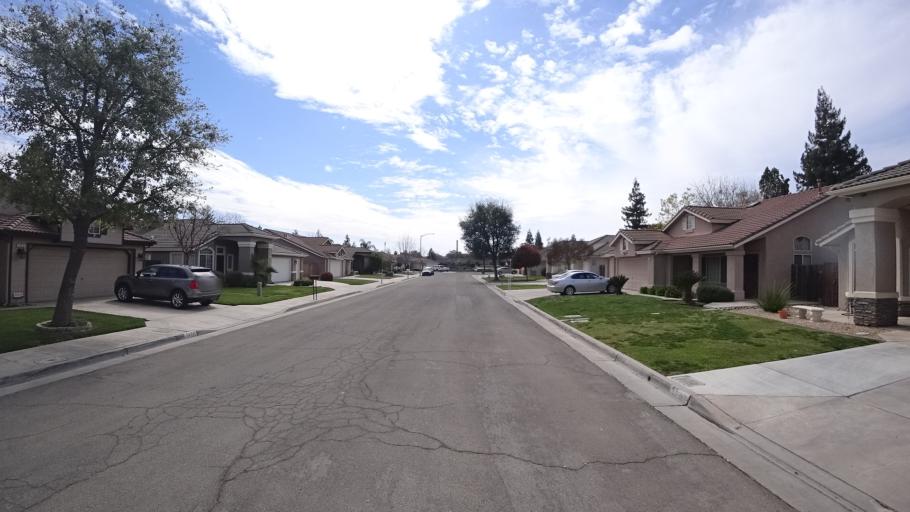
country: US
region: California
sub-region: Fresno County
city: Biola
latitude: 36.8403
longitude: -119.8888
